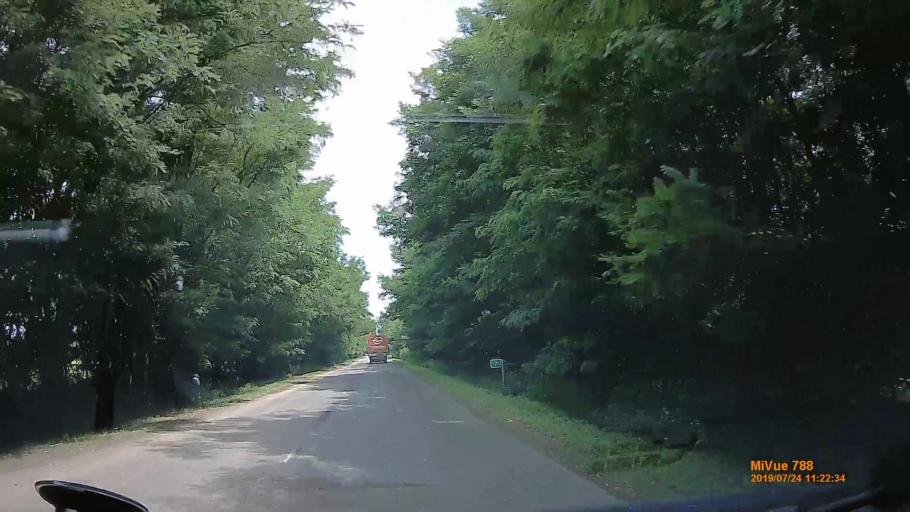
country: HU
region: Szabolcs-Szatmar-Bereg
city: Tarpa
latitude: 48.1789
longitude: 22.4639
